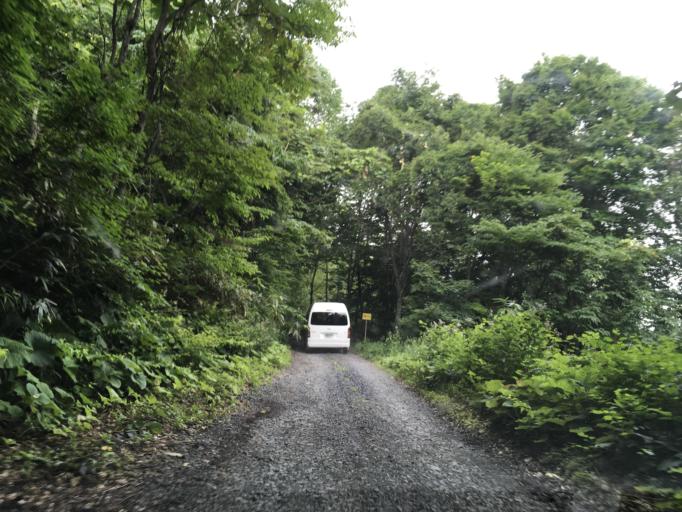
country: JP
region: Iwate
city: Ichinoseki
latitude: 38.9563
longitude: 140.8486
